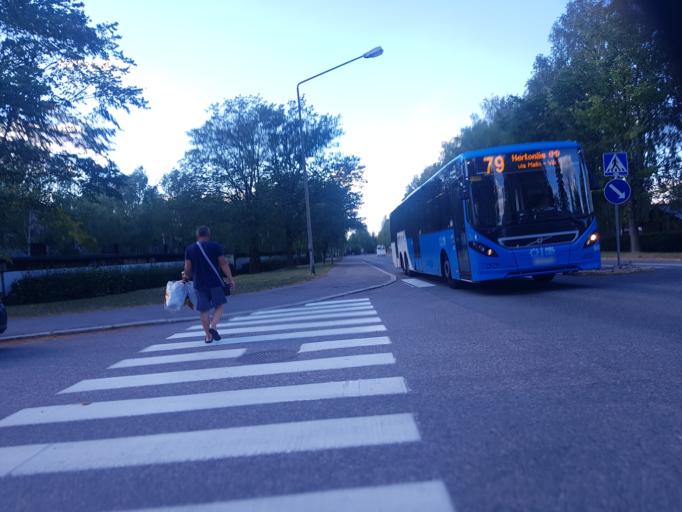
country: FI
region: Uusimaa
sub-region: Helsinki
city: Vantaa
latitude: 60.2735
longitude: 24.9925
